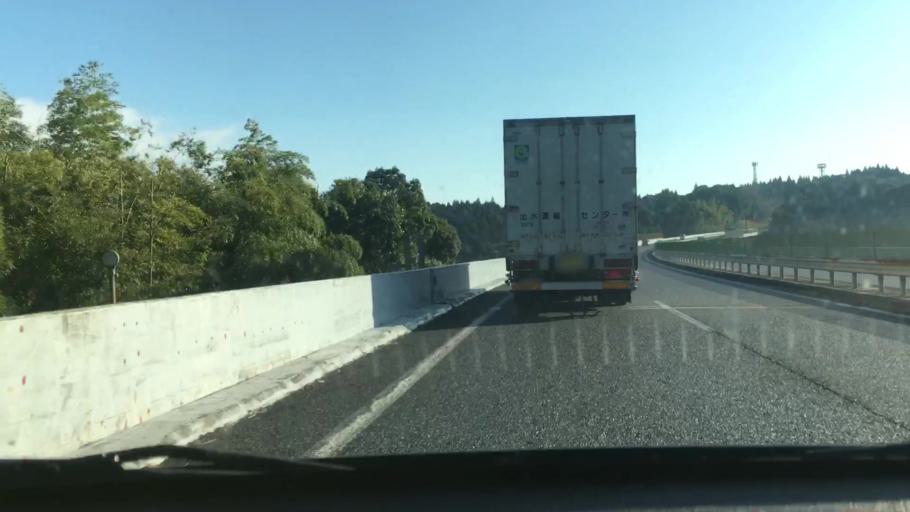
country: JP
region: Kagoshima
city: Kajiki
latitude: 31.9025
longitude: 130.7076
